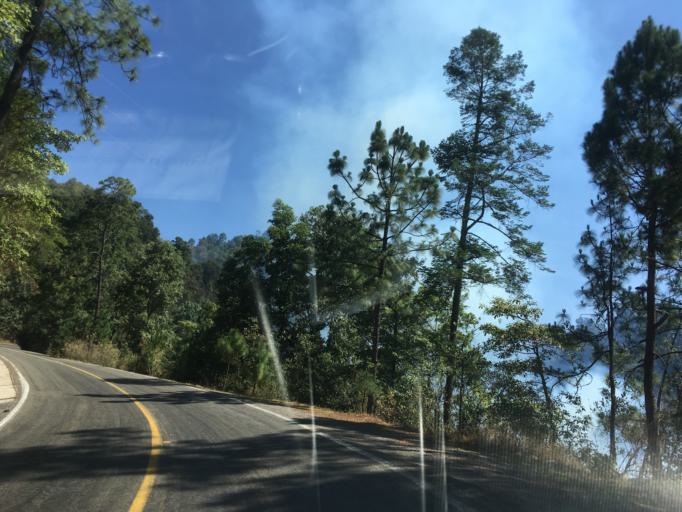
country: MX
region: Michoacan
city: Tzitzio
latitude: 19.6652
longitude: -100.9093
